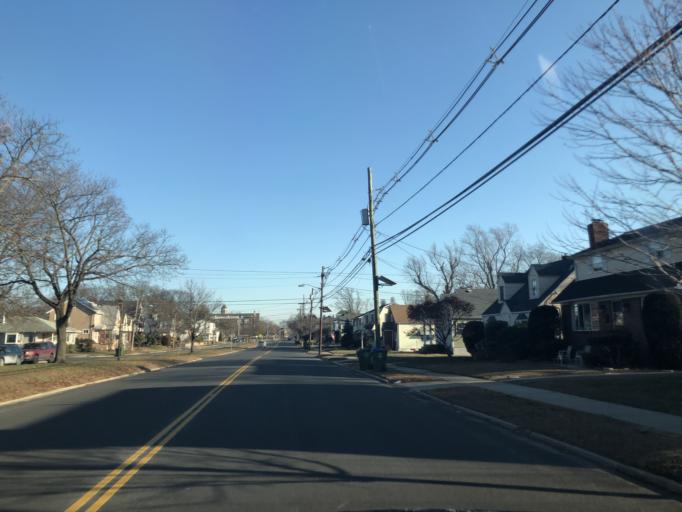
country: US
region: New Jersey
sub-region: Middlesex County
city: Fords
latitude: 40.5305
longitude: -74.3223
